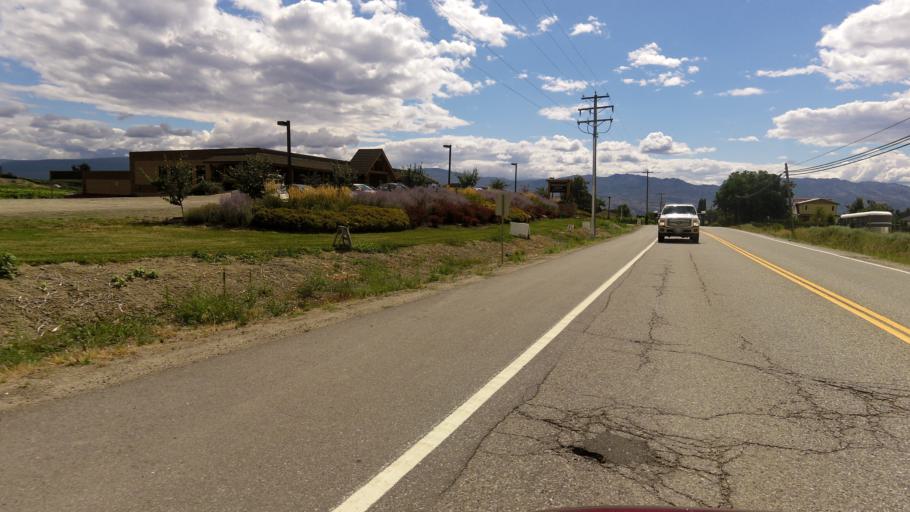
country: CA
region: British Columbia
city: West Kelowna
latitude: 49.8562
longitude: -119.5559
